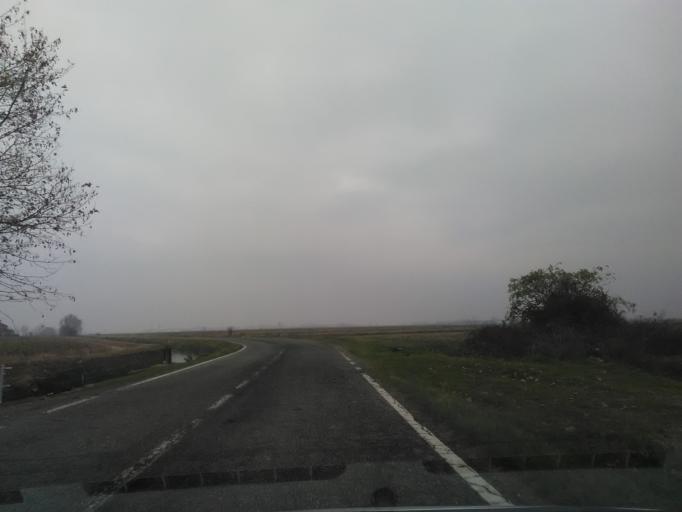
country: IT
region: Piedmont
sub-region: Provincia di Vercelli
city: Salasco
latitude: 45.3121
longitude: 8.2438
